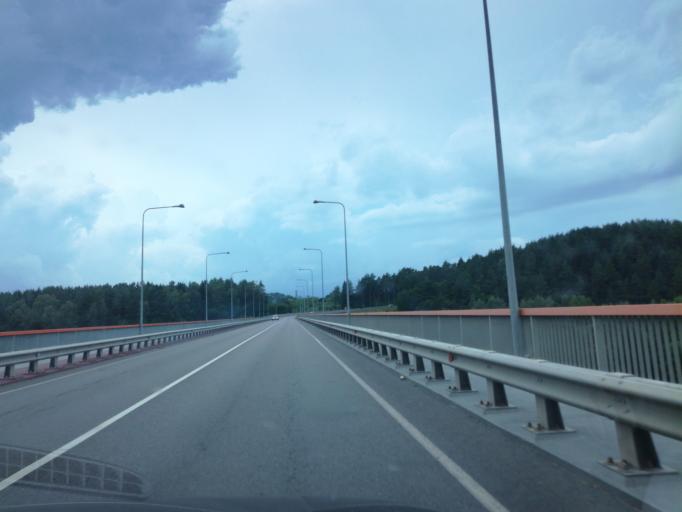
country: LT
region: Alytaus apskritis
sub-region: Alytus
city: Alytus
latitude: 54.4213
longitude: 24.0421
